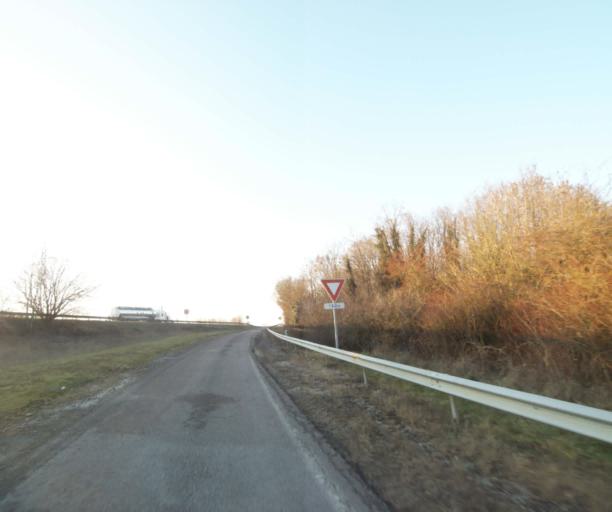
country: FR
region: Champagne-Ardenne
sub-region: Departement de la Haute-Marne
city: Chevillon
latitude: 48.5417
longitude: 5.0853
